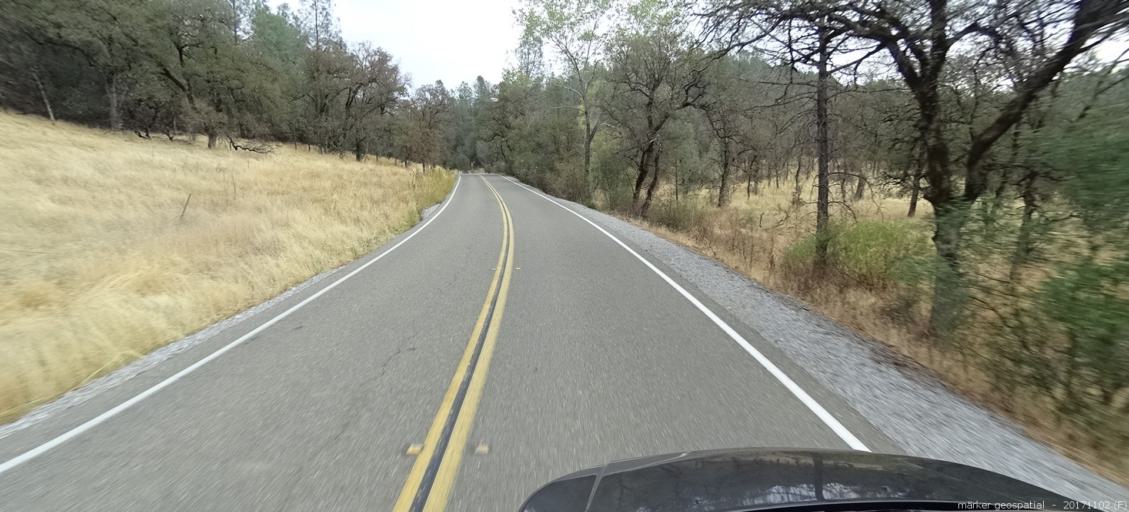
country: US
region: California
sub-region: Shasta County
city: Bella Vista
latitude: 40.7040
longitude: -122.2591
